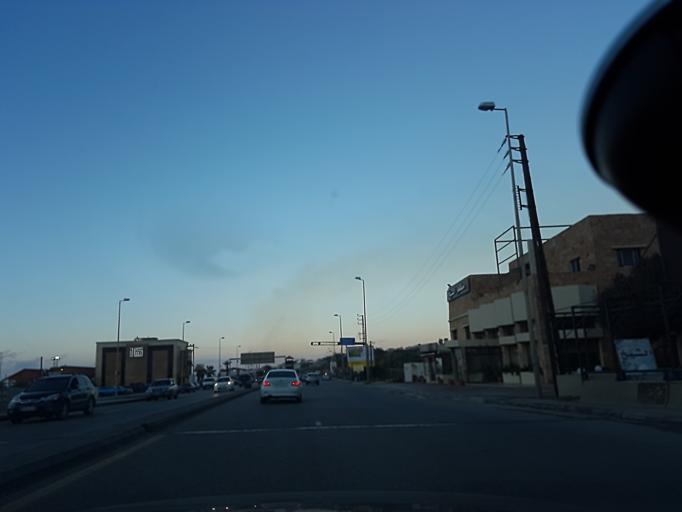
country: LB
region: Liban-Sud
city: Sidon
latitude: 33.5893
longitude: 35.3872
